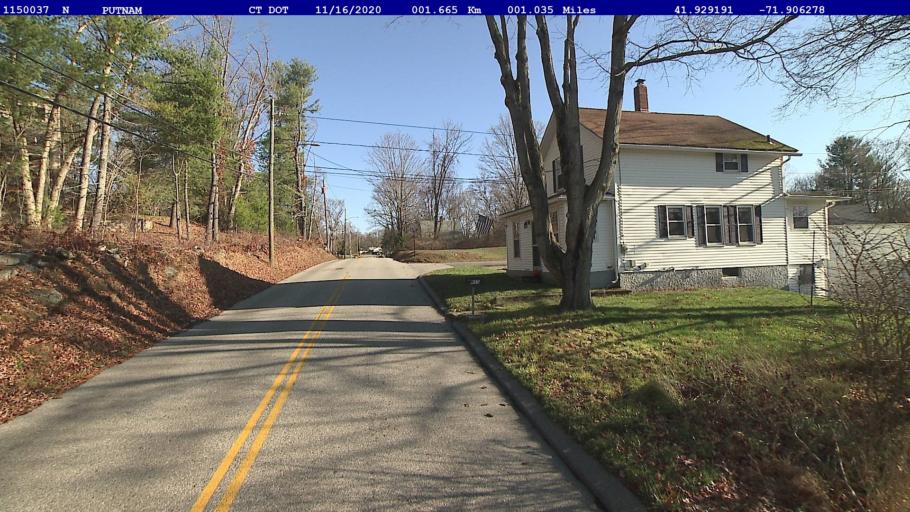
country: US
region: Connecticut
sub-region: Windham County
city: Putnam
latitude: 41.9292
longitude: -71.9063
